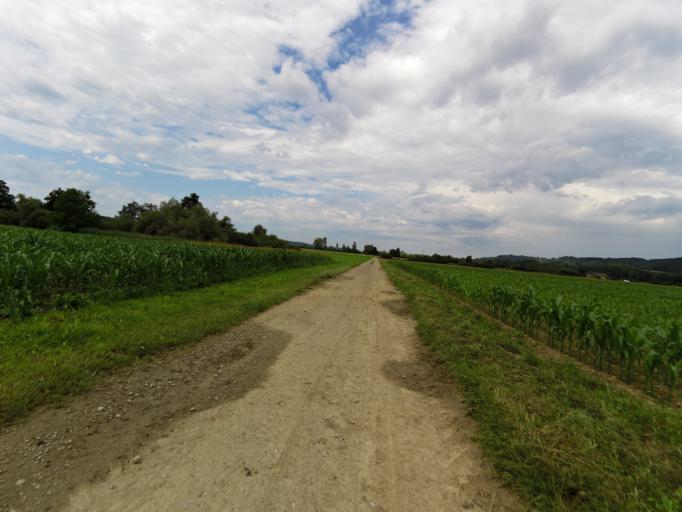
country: CH
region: Thurgau
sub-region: Frauenfeld District
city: Frauenfeld
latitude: 47.5695
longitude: 8.8743
